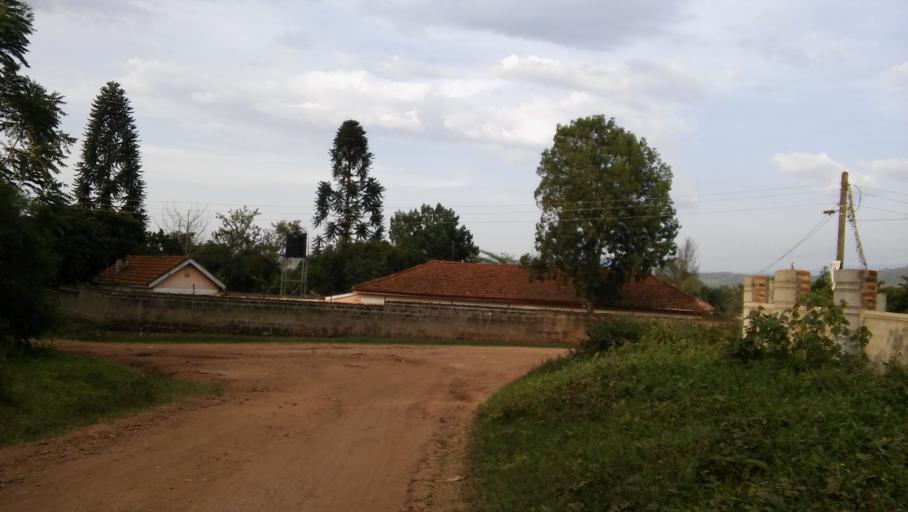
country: UG
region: Eastern Region
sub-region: Mbale District
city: Mbale
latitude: 1.0686
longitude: 34.1890
